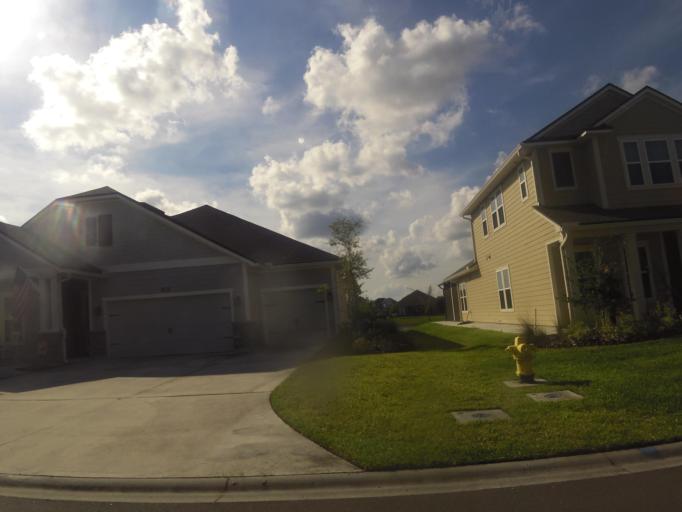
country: US
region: Florida
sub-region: Saint Johns County
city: Saint Augustine
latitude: 29.9264
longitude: -81.4899
